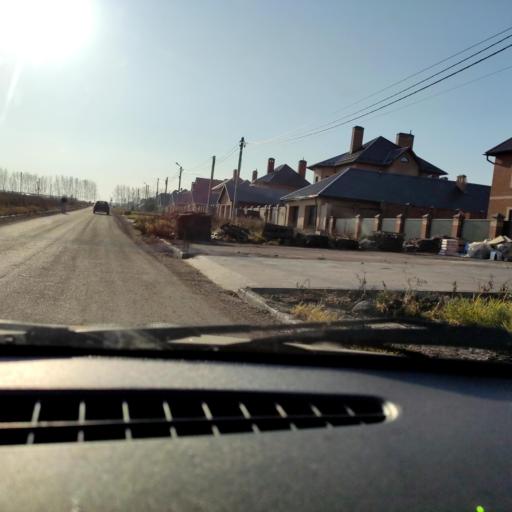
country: RU
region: Bashkortostan
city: Kabakovo
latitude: 54.6195
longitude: 56.1418
